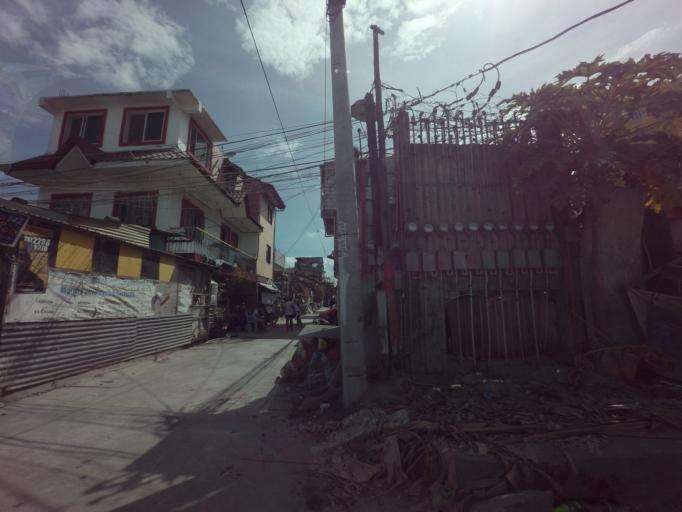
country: PH
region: Calabarzon
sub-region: Province of Rizal
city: Taguig
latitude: 14.5276
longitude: 121.0881
